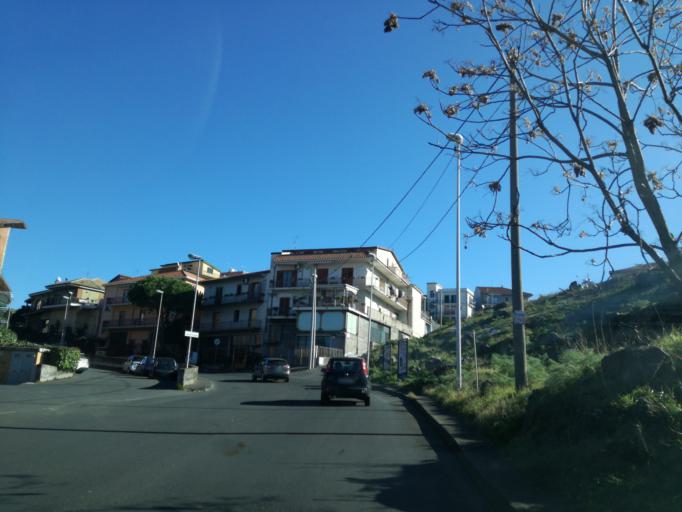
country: IT
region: Sicily
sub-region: Catania
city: Bronte
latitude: 37.7907
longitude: 14.8408
